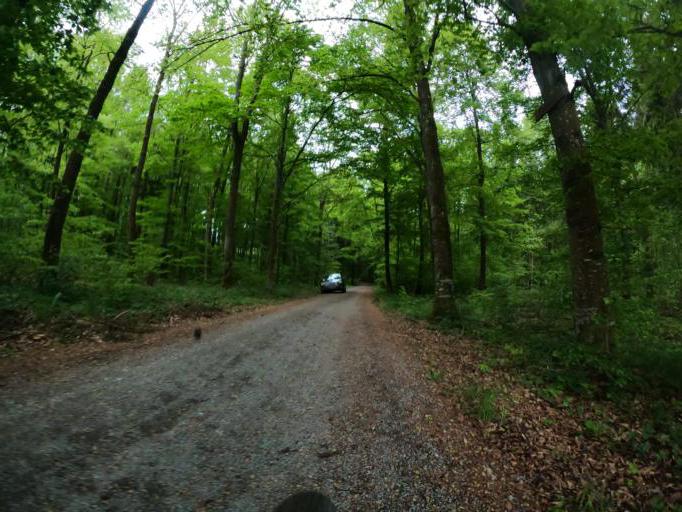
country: DE
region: Baden-Wuerttemberg
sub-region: Regierungsbezirk Stuttgart
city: Aidlingen
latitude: 48.6972
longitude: 8.9137
